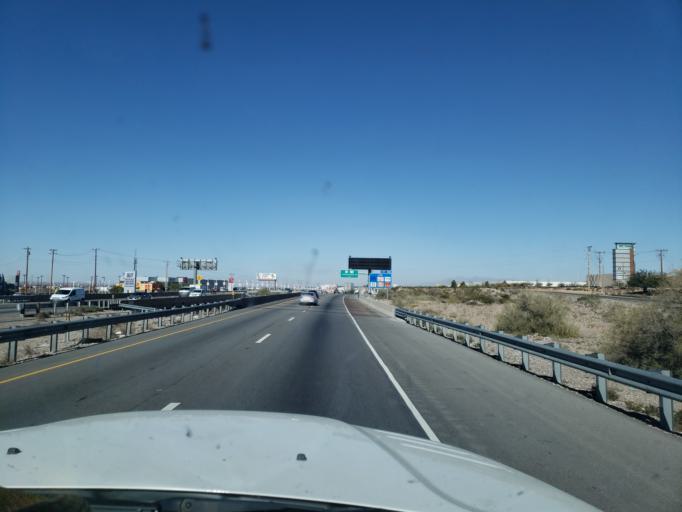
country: US
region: Texas
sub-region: El Paso County
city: Canutillo
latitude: 31.8849
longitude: -106.5822
